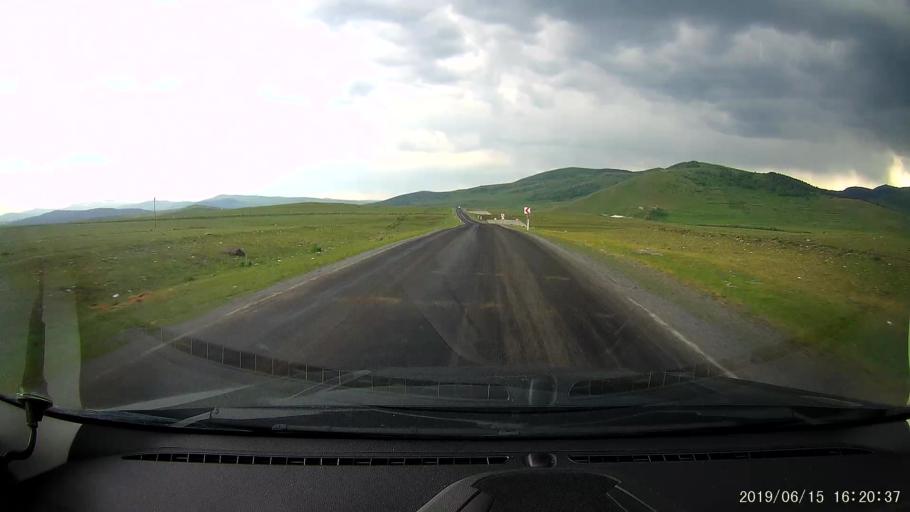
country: TR
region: Ardahan
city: Hanak
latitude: 41.2112
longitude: 42.8469
